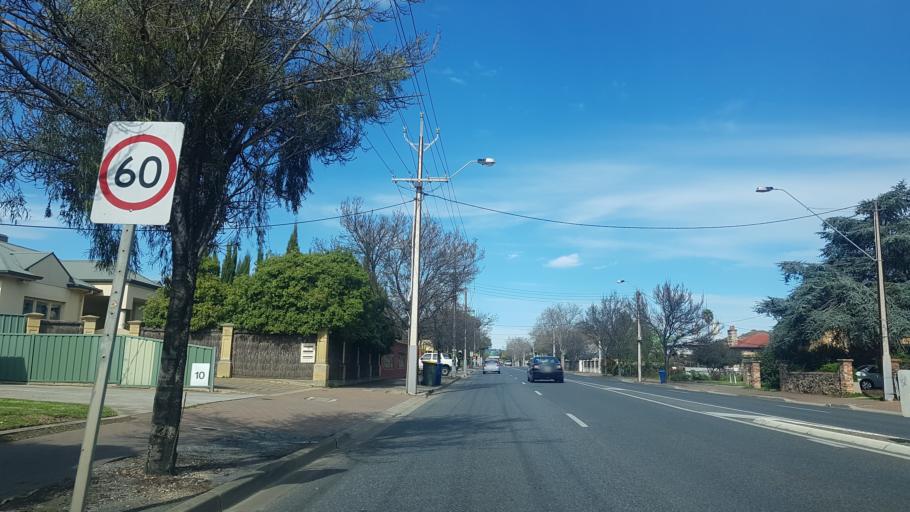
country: AU
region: South Australia
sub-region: Unley
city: Millswood
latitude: -34.9607
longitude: 138.5904
